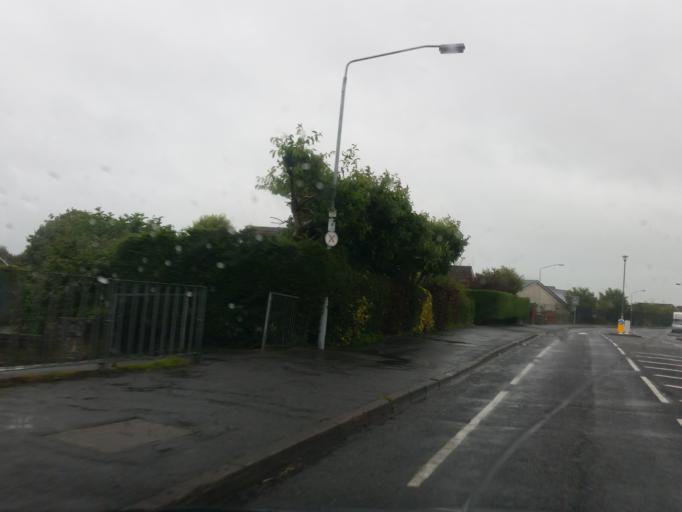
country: GB
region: Northern Ireland
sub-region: North Down District
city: Bangor
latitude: 54.6518
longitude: -5.6331
